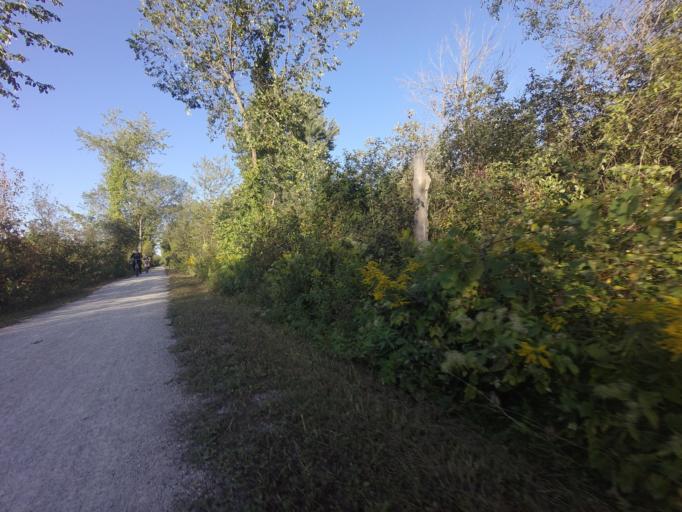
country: CA
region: Ontario
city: Orangeville
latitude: 43.8164
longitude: -79.9265
